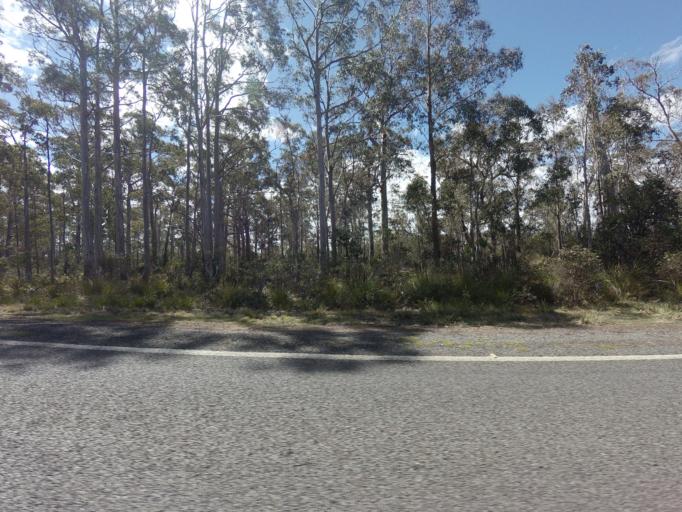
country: AU
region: Tasmania
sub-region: Northern Midlands
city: Evandale
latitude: -42.0250
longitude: 147.8428
